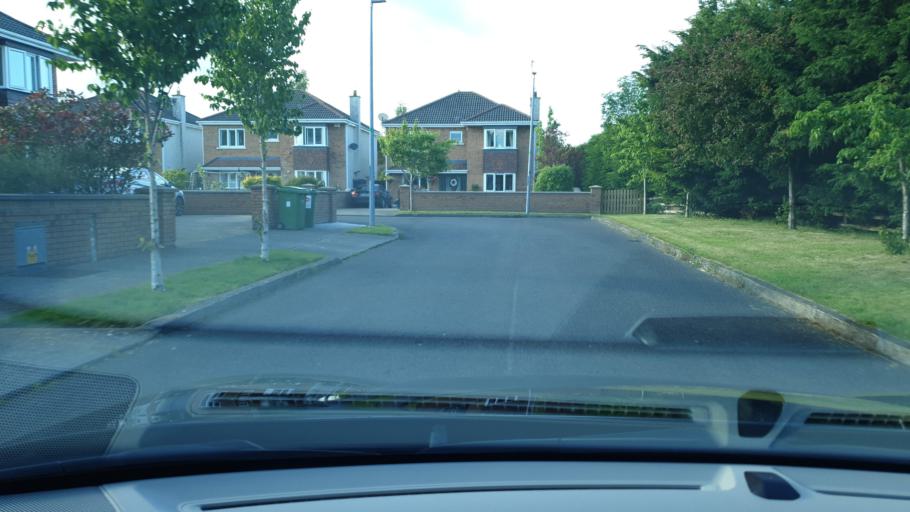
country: IE
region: Leinster
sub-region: An Mhi
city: Ashbourne
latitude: 53.5189
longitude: -6.4003
